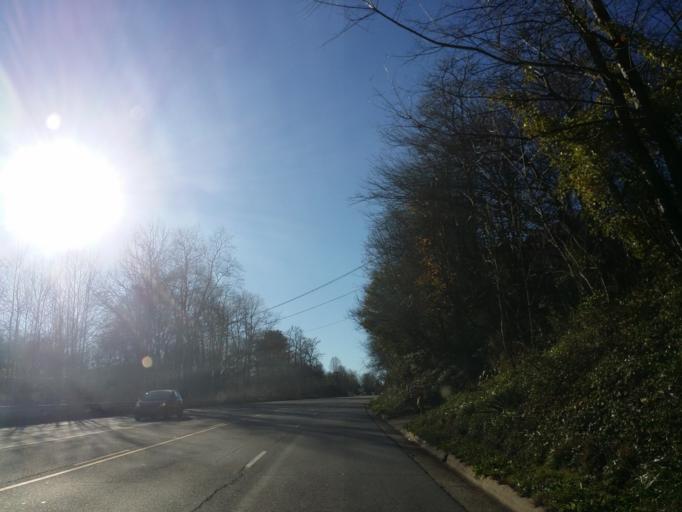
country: US
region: North Carolina
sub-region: Buncombe County
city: Swannanoa
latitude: 35.5975
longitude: -82.4144
